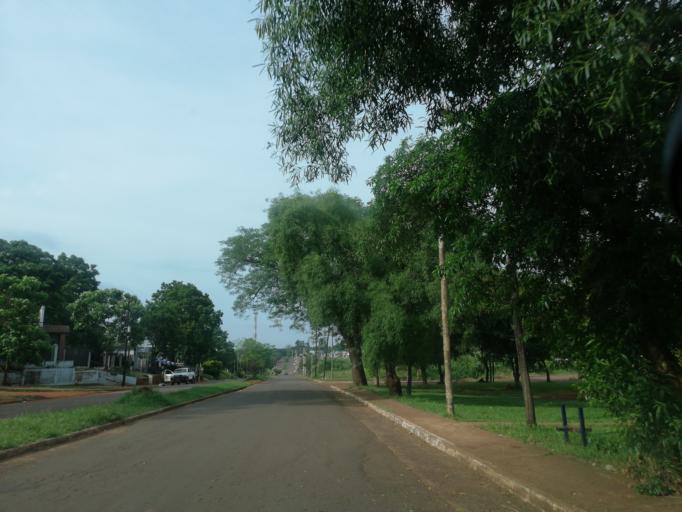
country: AR
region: Misiones
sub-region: Departamento de Capital
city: Posadas
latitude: -27.4123
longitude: -55.9168
